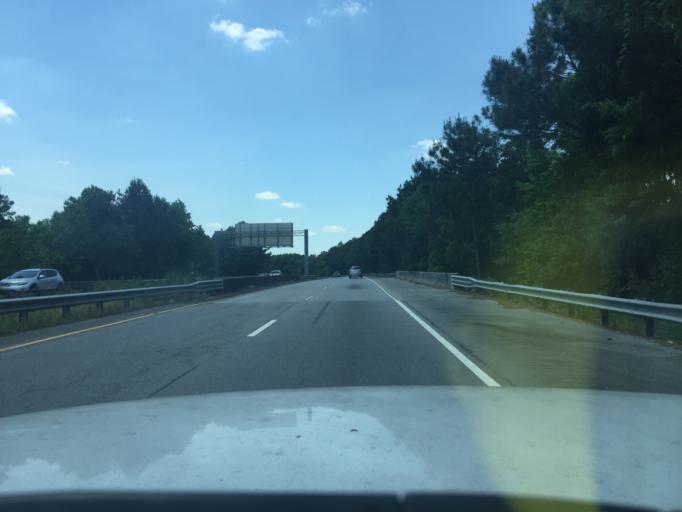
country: US
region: Georgia
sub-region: Chatham County
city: Savannah
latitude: 32.0425
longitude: -81.1561
